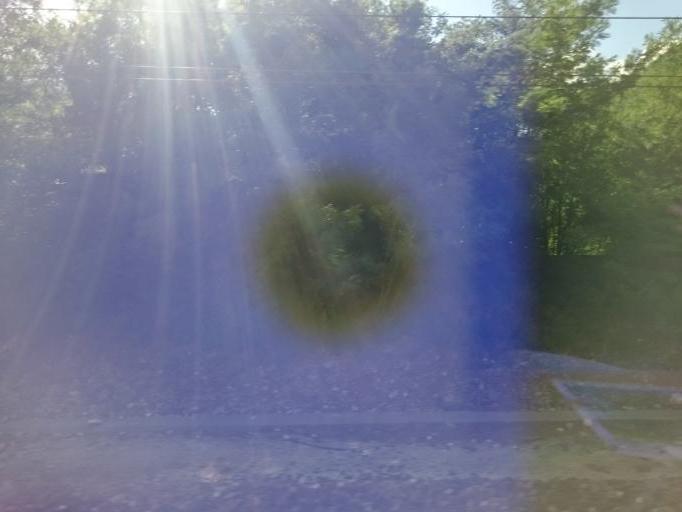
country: IT
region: Trentino-Alto Adige
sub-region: Provincia di Trento
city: Ala
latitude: 45.7623
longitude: 10.9985
